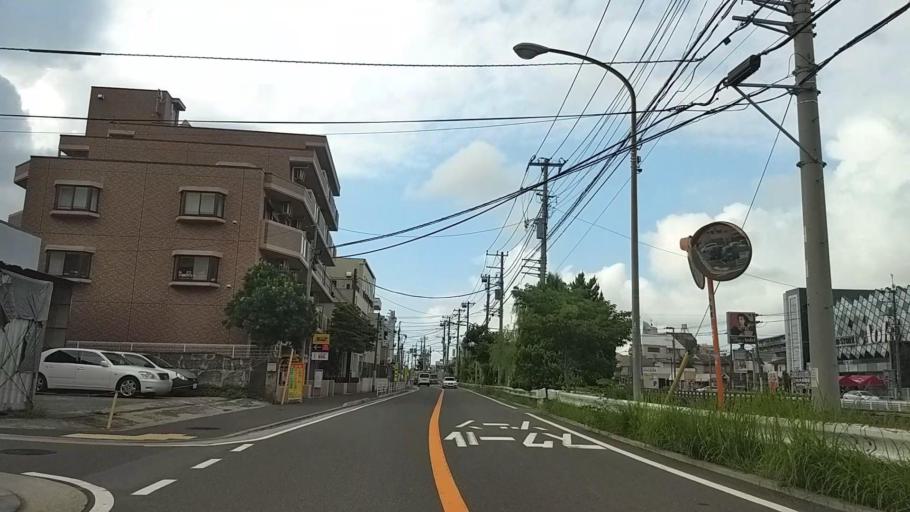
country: JP
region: Kanagawa
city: Yokohama
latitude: 35.4277
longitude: 139.6229
